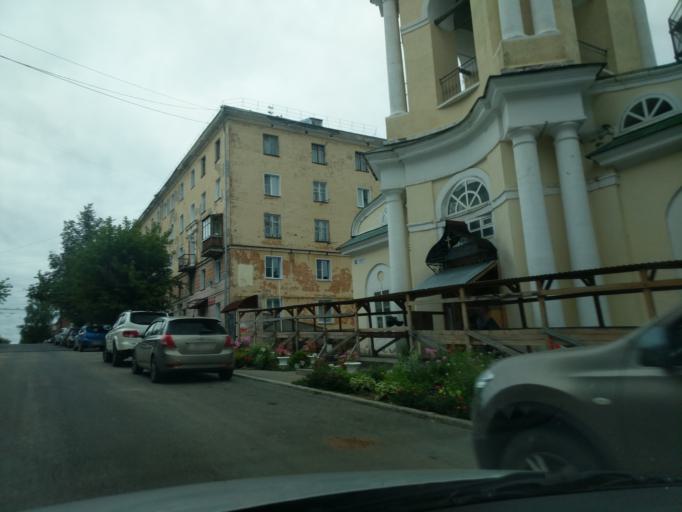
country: RU
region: Kirov
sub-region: Kirovo-Chepetskiy Rayon
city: Kirov
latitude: 58.6029
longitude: 49.6769
